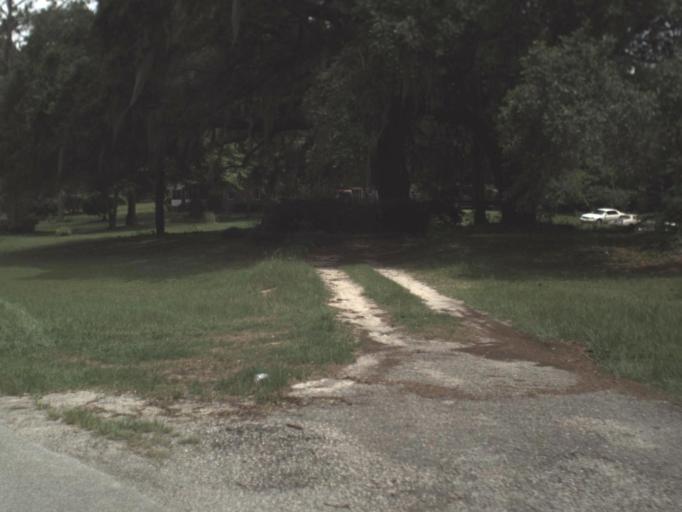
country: US
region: Florida
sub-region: Madison County
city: Madison
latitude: 30.4723
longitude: -83.3550
